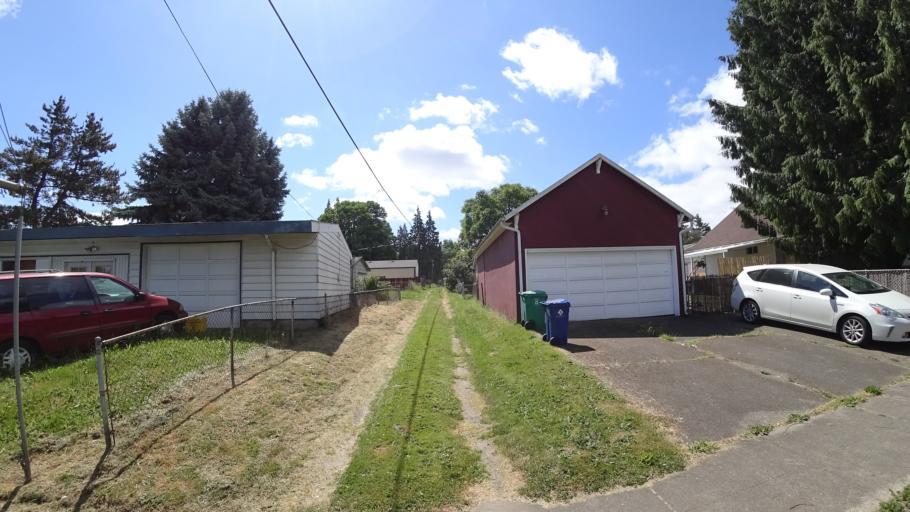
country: US
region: Oregon
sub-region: Washington County
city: West Haven
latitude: 45.5991
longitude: -122.7589
